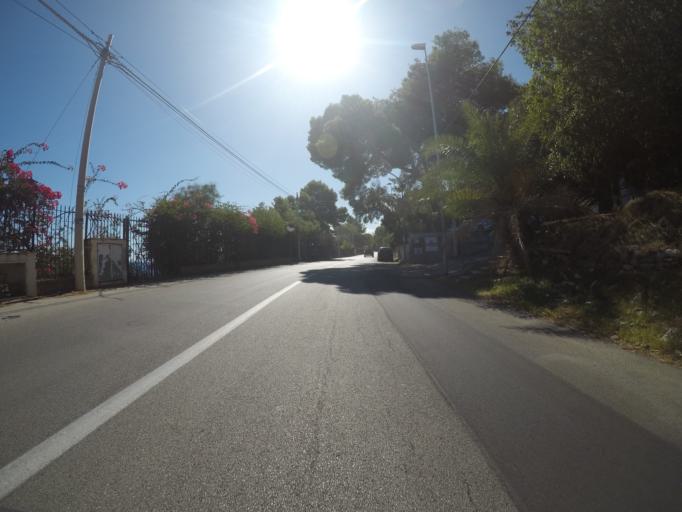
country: IT
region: Sicily
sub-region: Palermo
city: Palermo
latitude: 38.1833
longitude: 13.3642
